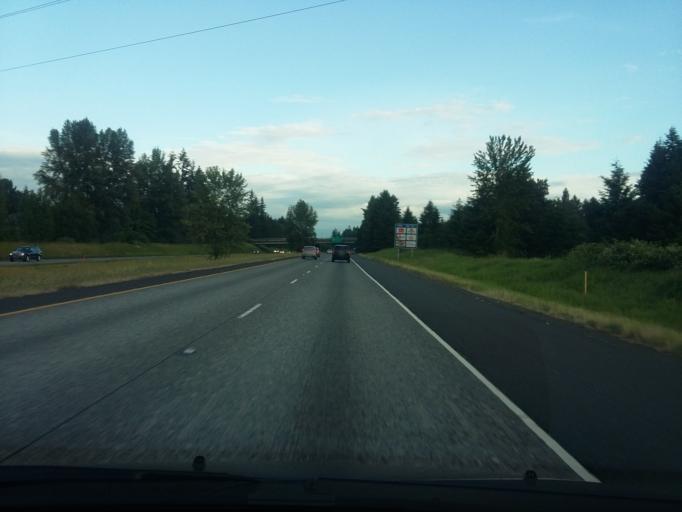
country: US
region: Washington
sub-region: Clark County
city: Five Corners
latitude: 45.6709
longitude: -122.5819
